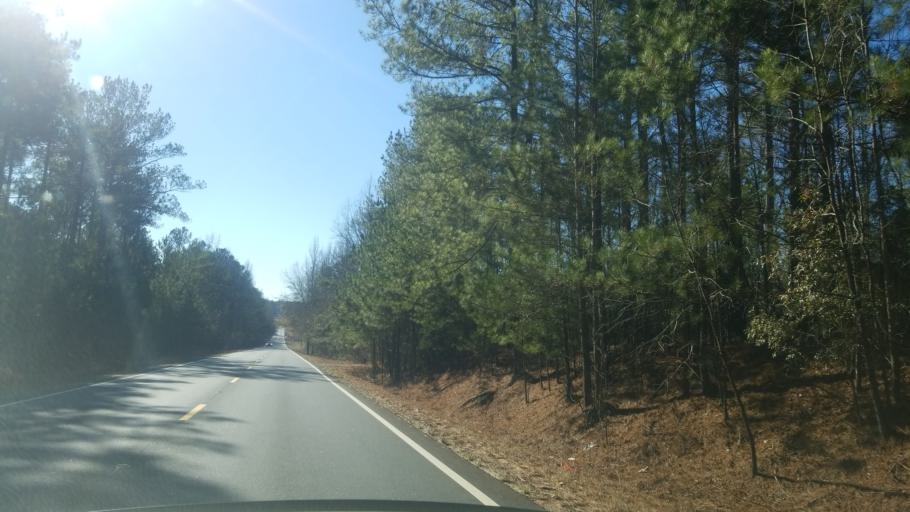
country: US
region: Alabama
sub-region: Chambers County
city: Valley
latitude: 32.8009
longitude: -85.1028
